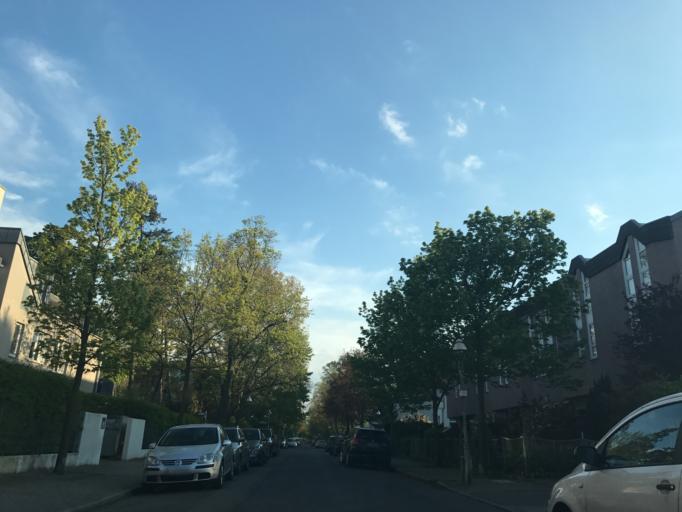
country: DE
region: Berlin
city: Westend
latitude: 52.5150
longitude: 13.2764
